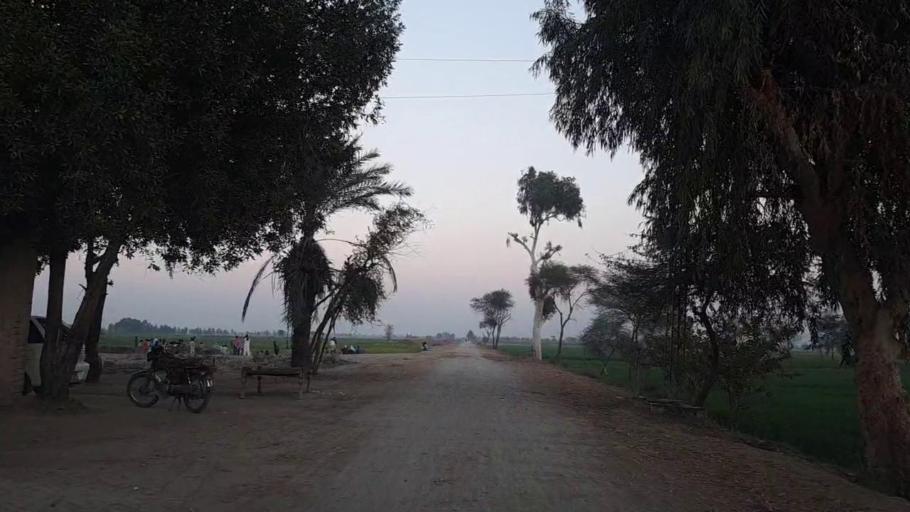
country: PK
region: Sindh
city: Naushahro Firoz
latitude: 26.7896
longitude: 68.0454
